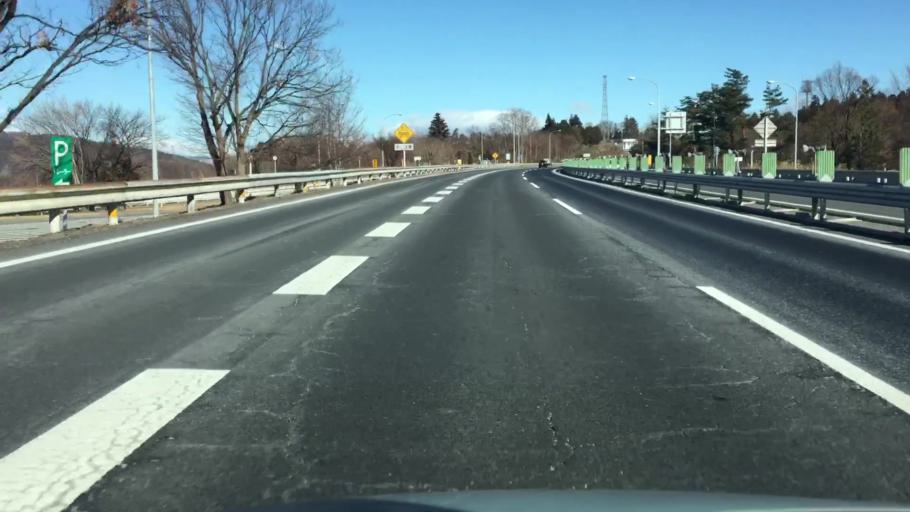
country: JP
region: Gunma
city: Shibukawa
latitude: 36.5376
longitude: 139.0482
